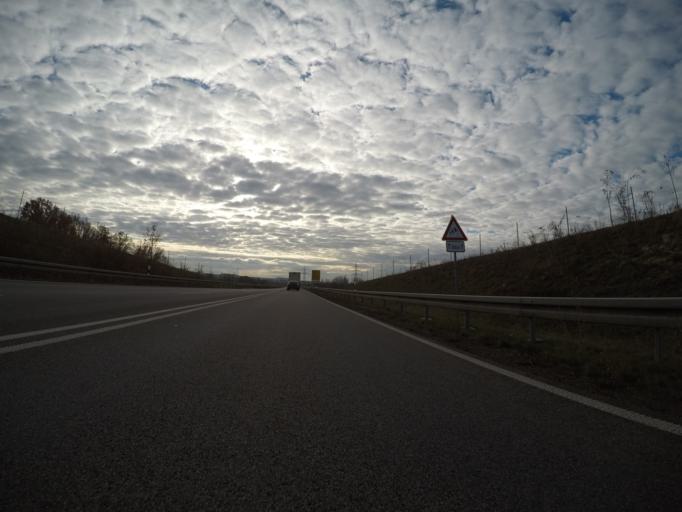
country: DE
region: Thuringia
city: Gossnitz
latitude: 50.8790
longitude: 12.4407
